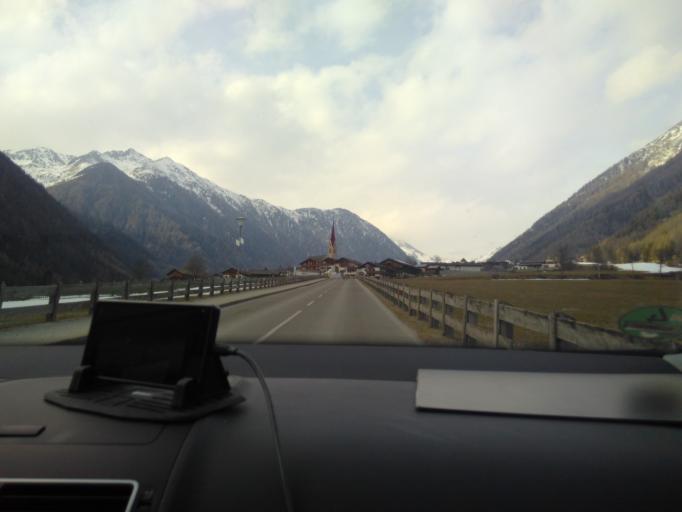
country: IT
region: Trentino-Alto Adige
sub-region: Bolzano
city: Fortezza
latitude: 46.8359
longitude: 11.6290
